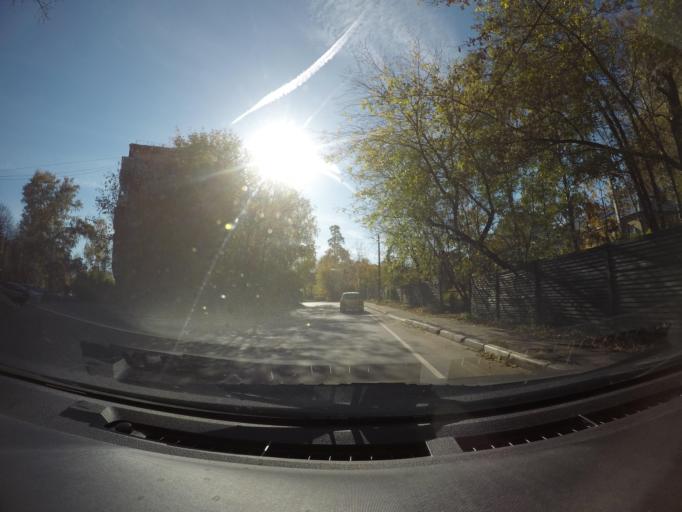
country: RU
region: Moskovskaya
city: Rodniki
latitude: 55.6405
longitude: 38.0532
